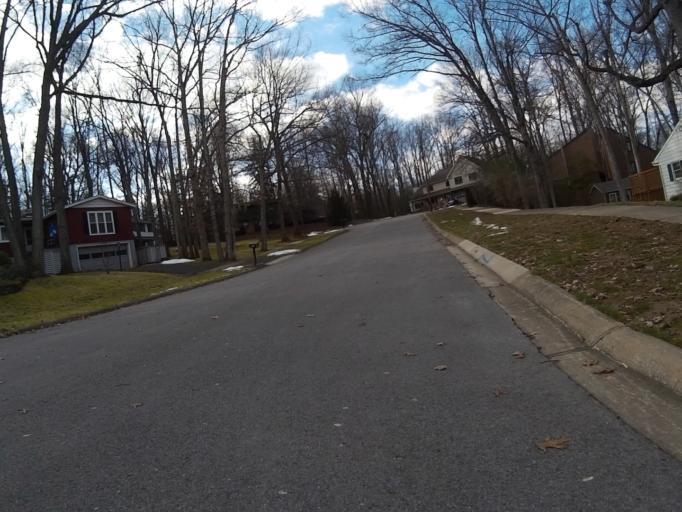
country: US
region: Pennsylvania
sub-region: Centre County
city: Park Forest Village
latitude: 40.8025
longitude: -77.9077
